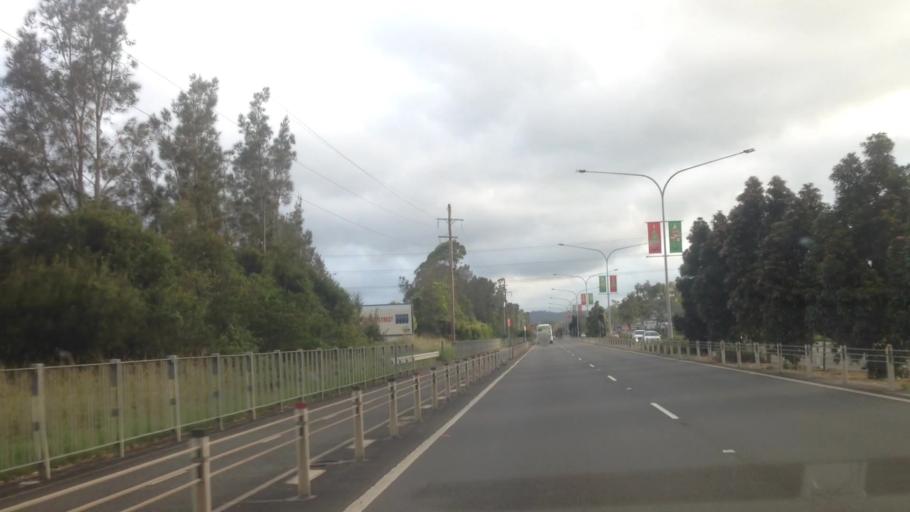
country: AU
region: New South Wales
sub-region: Wyong Shire
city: Chittaway Bay
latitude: -33.2973
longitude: 151.4222
